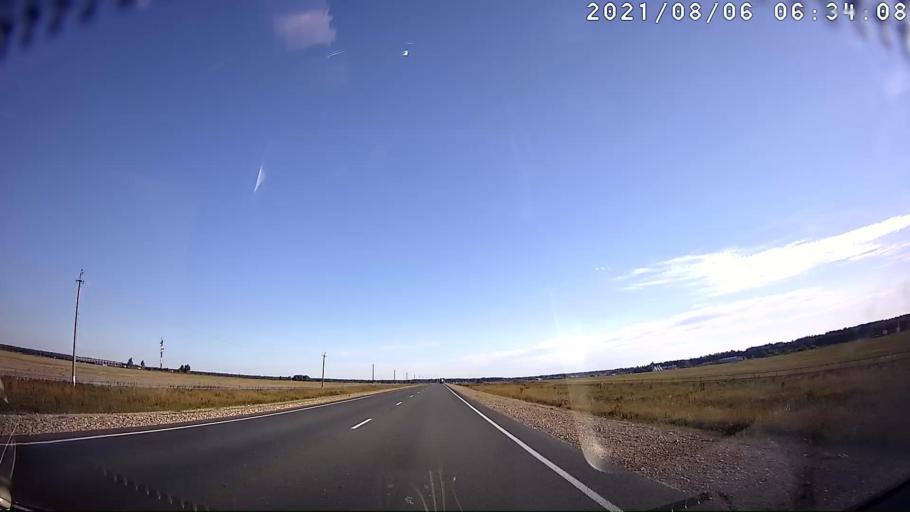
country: RU
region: Mariy-El
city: Krasnogorskiy
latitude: 56.2015
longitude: 48.2361
